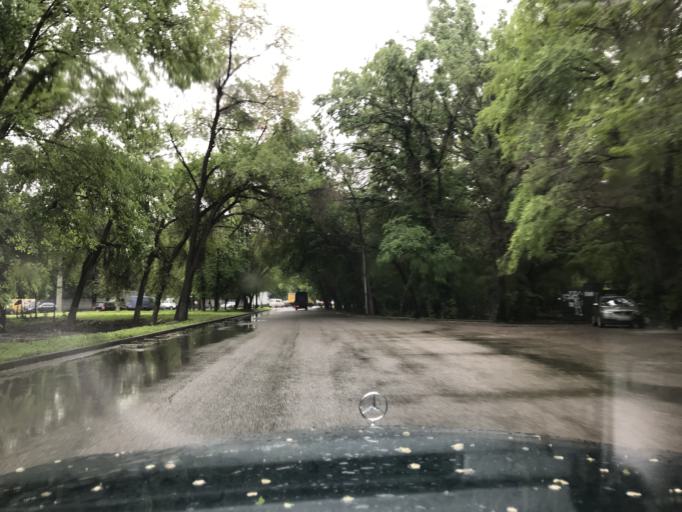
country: KZ
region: Almaty Oblysy
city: Pervomayskiy
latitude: 43.3302
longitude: 76.9592
